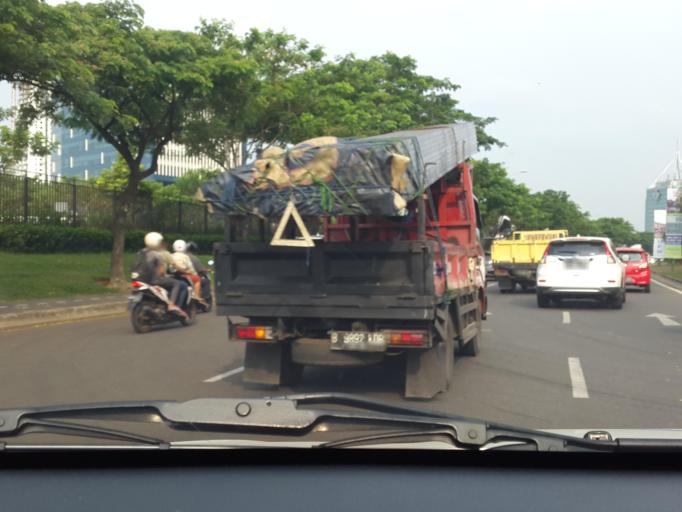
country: ID
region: Banten
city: South Tangerang
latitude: -6.2746
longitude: 106.7189
